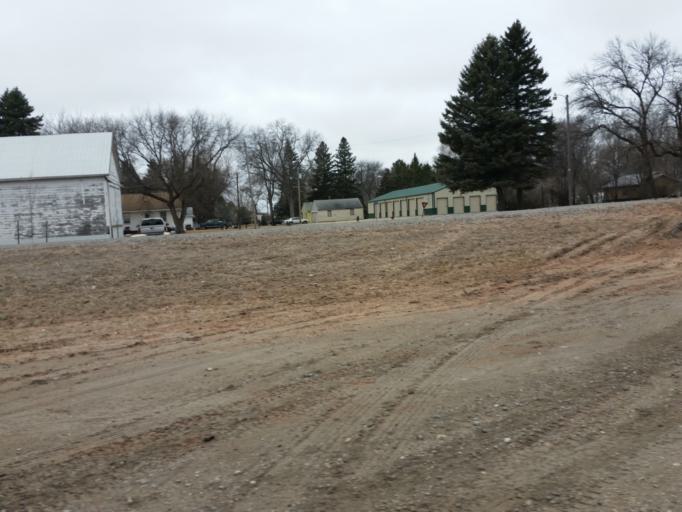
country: US
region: North Dakota
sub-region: Traill County
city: Hillsboro
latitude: 47.1885
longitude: -97.2179
